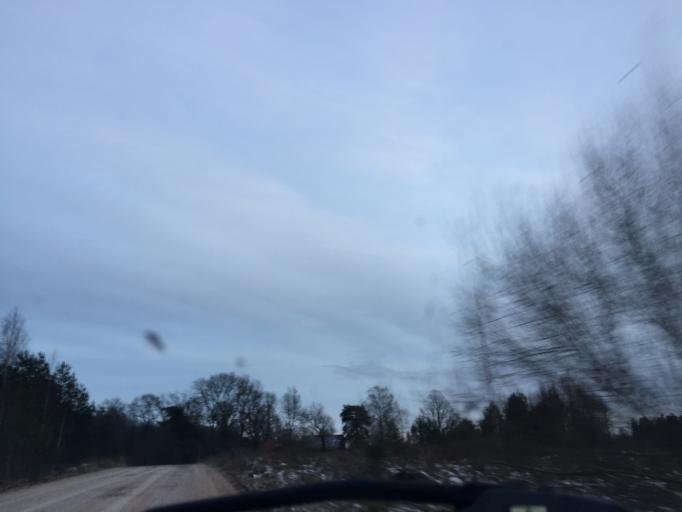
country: LV
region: Burtnieki
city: Matisi
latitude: 57.6363
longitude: 25.0707
